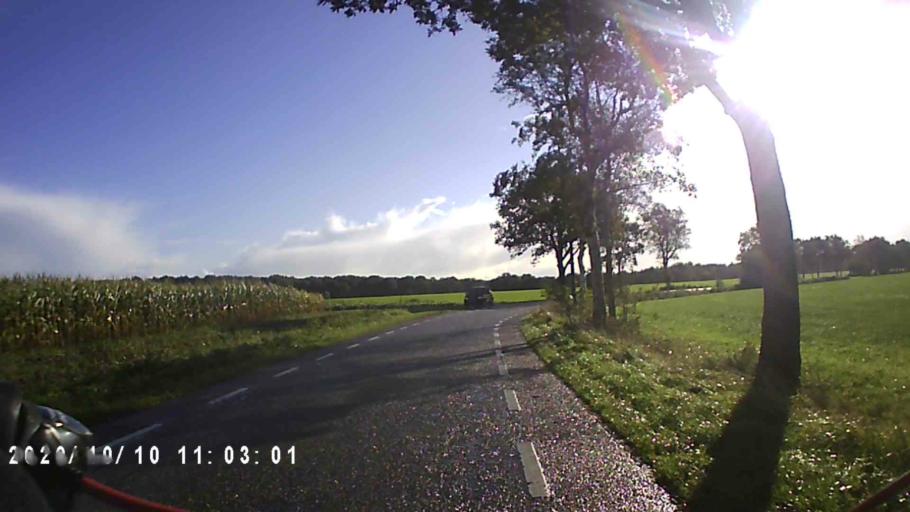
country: NL
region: Friesland
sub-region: Gemeente Achtkarspelen
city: Surhuisterveen
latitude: 53.1356
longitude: 6.2211
